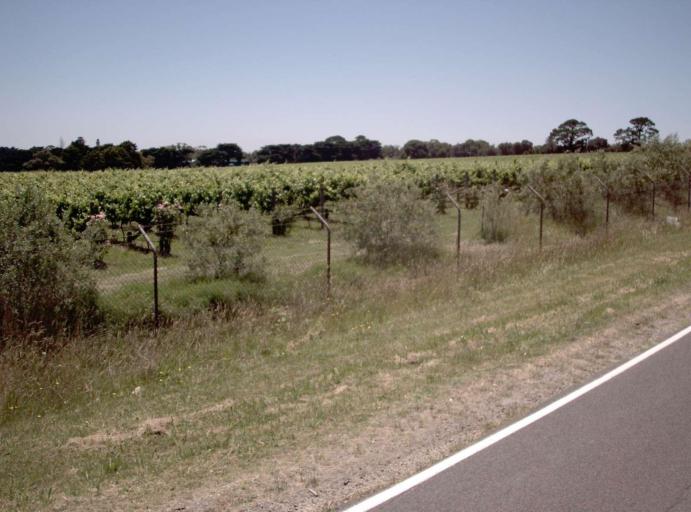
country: AU
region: Victoria
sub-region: Mornington Peninsula
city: Mornington
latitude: -38.2112
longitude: 145.0683
